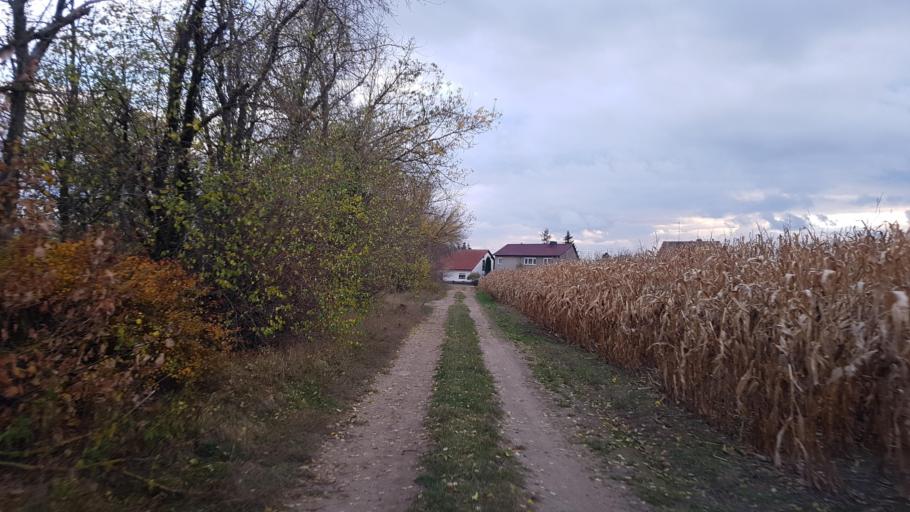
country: DE
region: Saxony-Anhalt
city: Seyda
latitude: 51.9262
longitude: 12.8868
